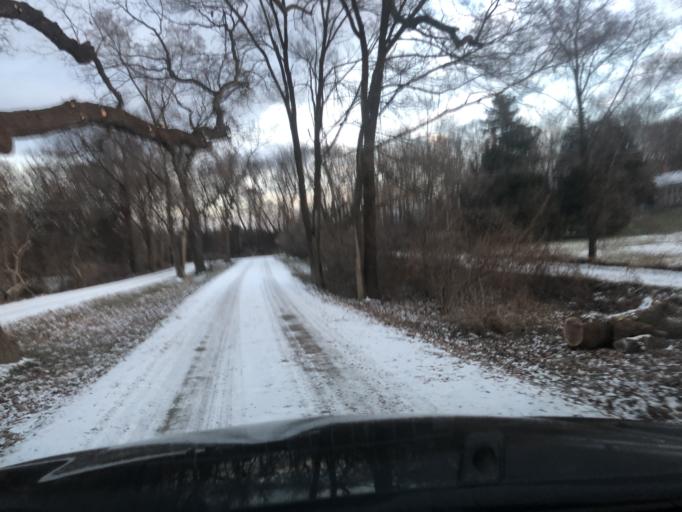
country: US
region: Michigan
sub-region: Oakland County
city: Milford
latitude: 42.5895
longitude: -83.6415
